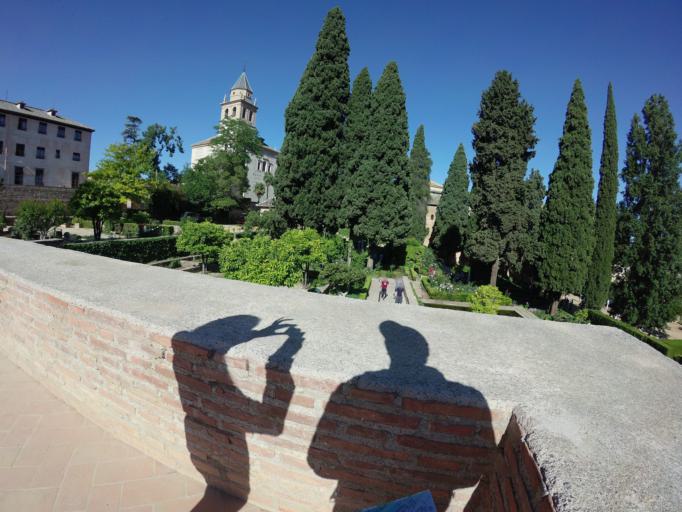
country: ES
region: Andalusia
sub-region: Provincia de Granada
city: Granada
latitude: 37.1768
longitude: -3.5882
